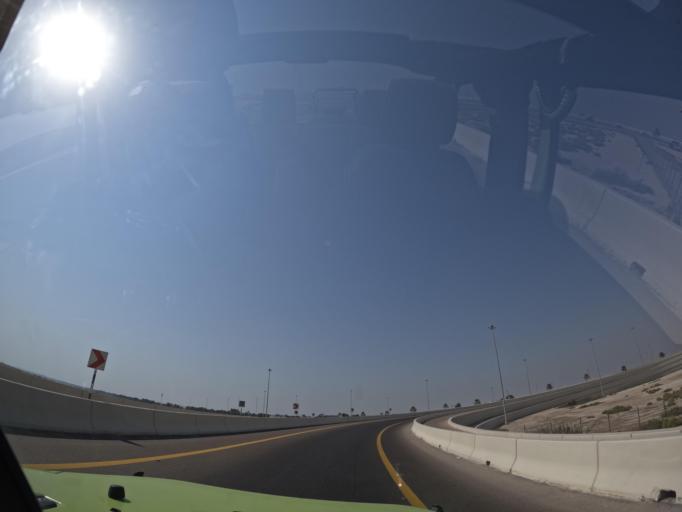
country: AE
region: Abu Dhabi
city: Abu Dhabi
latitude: 24.4066
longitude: 54.6695
